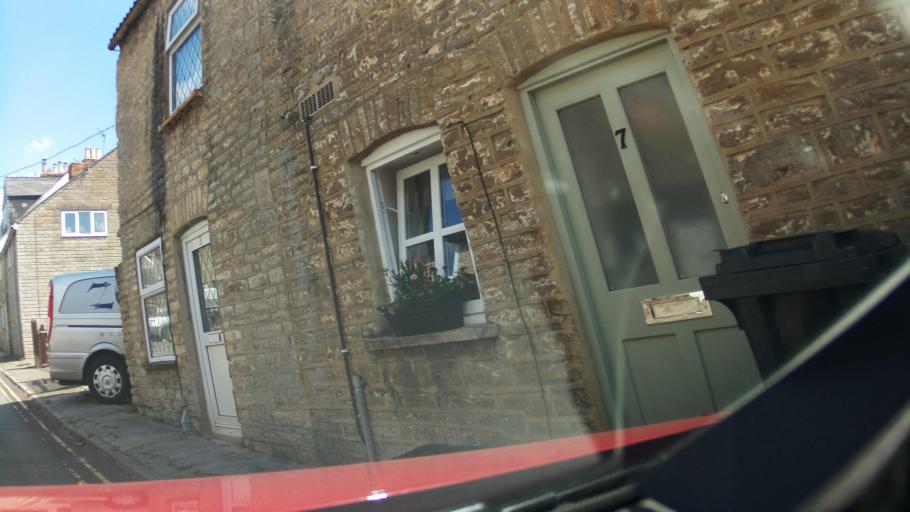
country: GB
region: England
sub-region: Wiltshire
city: Malmesbury
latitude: 51.5856
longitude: -2.1053
